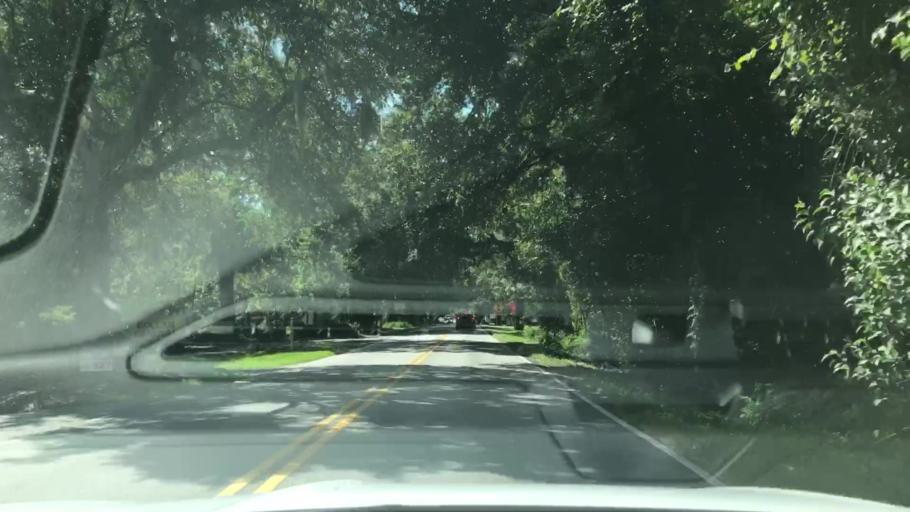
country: US
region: South Carolina
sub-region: Charleston County
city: North Charleston
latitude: 32.8233
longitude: -80.0376
